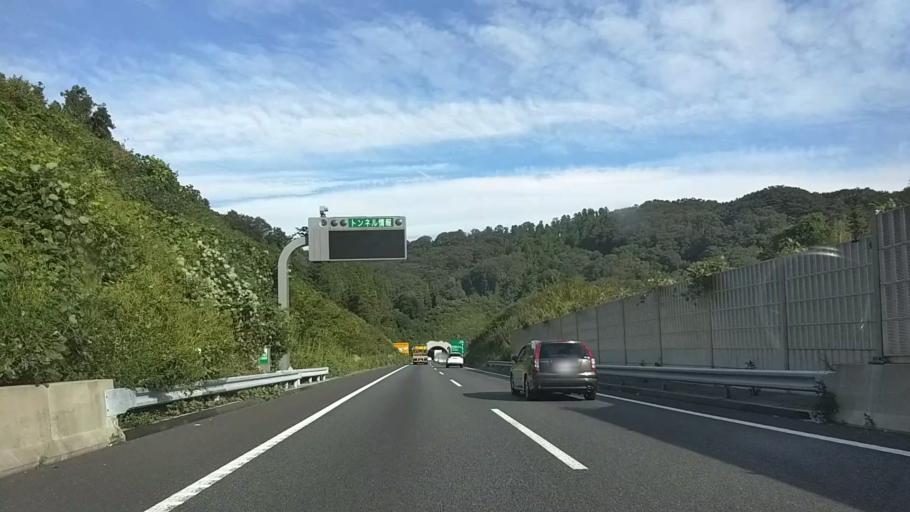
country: JP
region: Tokyo
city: Hachioji
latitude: 35.5572
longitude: 139.3140
